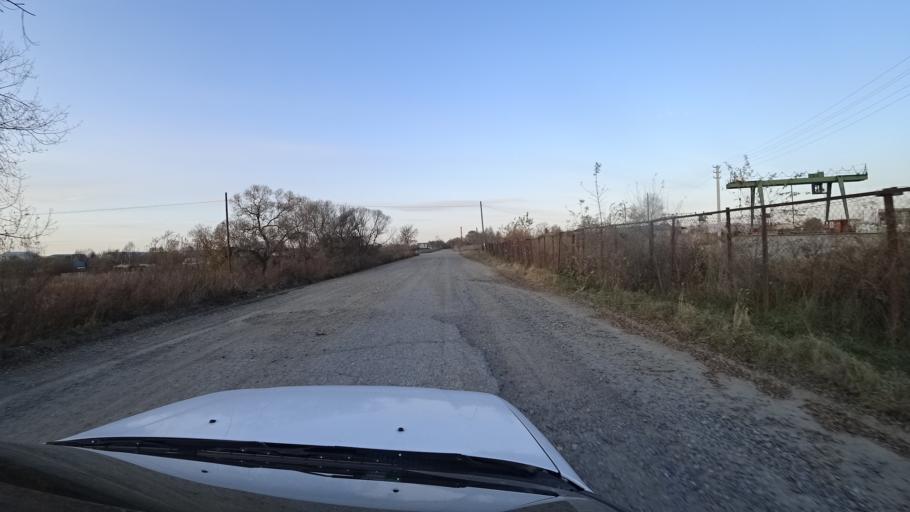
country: RU
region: Primorskiy
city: Dal'nerechensk
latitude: 45.9377
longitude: 133.8202
